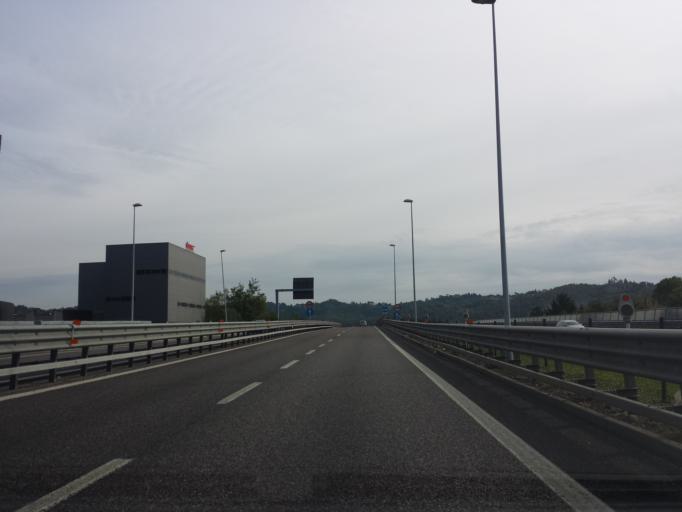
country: IT
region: Veneto
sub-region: Provincia di Vicenza
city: Creazzo
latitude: 45.5182
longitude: 11.5093
